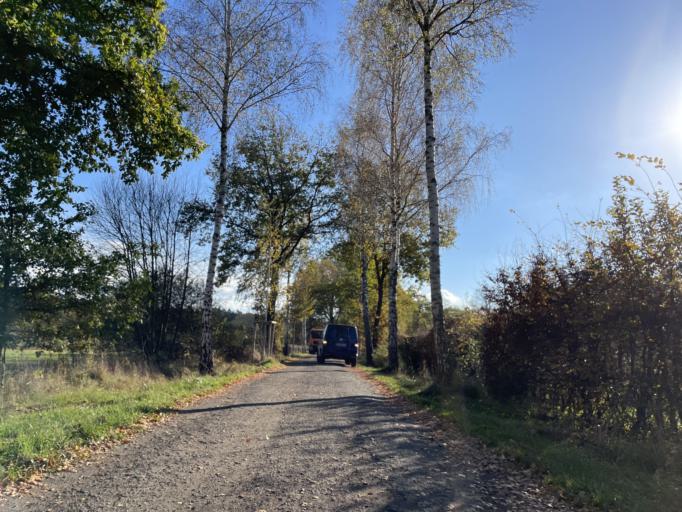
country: DE
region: Lower Saxony
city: Deutsch Evern
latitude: 53.2224
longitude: 10.4182
